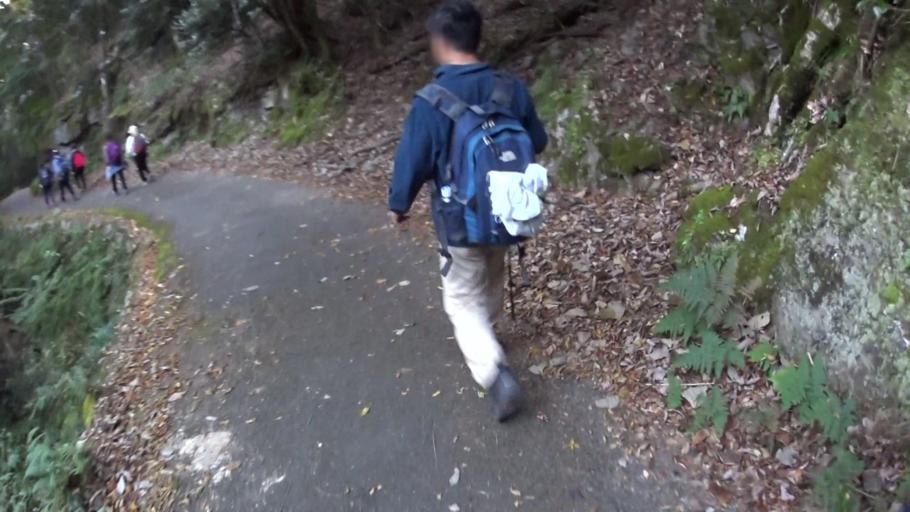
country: JP
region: Kyoto
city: Kameoka
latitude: 35.0468
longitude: 135.6540
